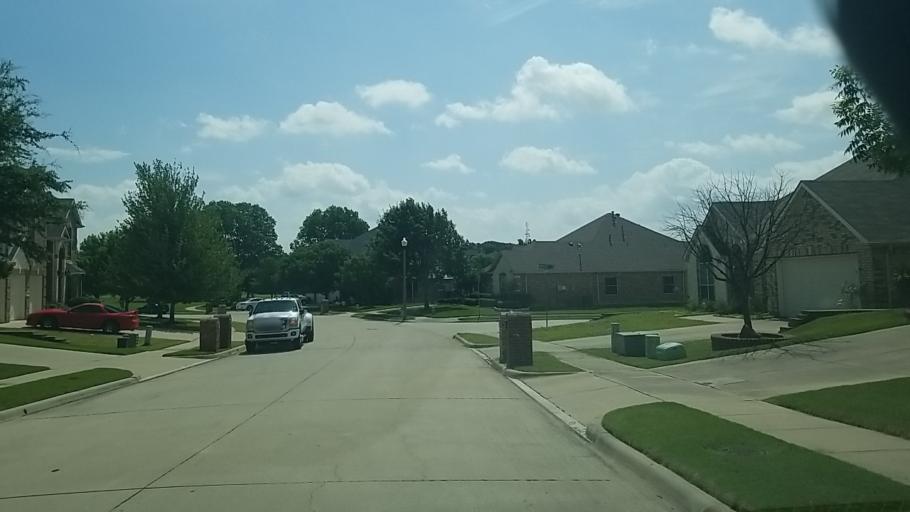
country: US
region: Texas
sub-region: Denton County
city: Corinth
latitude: 33.1459
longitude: -97.0955
